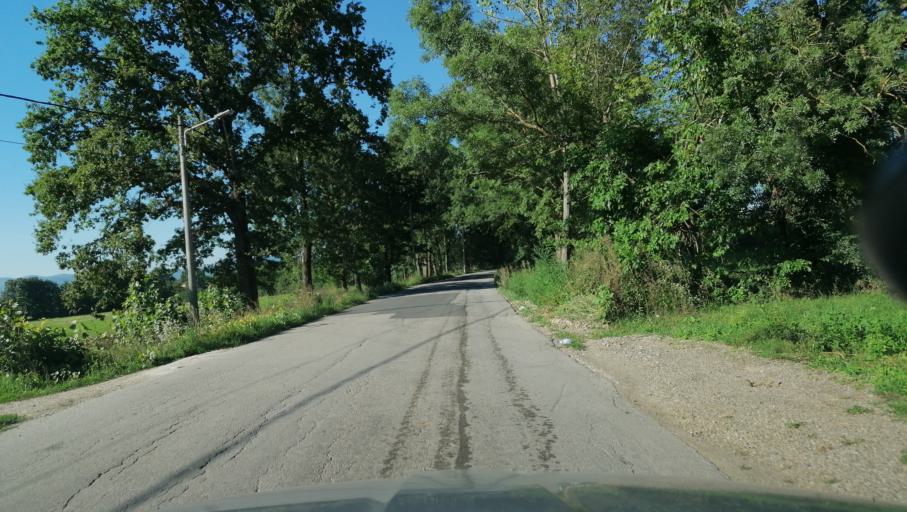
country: RS
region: Central Serbia
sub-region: Raski Okrug
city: Kraljevo
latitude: 43.8350
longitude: 20.5949
